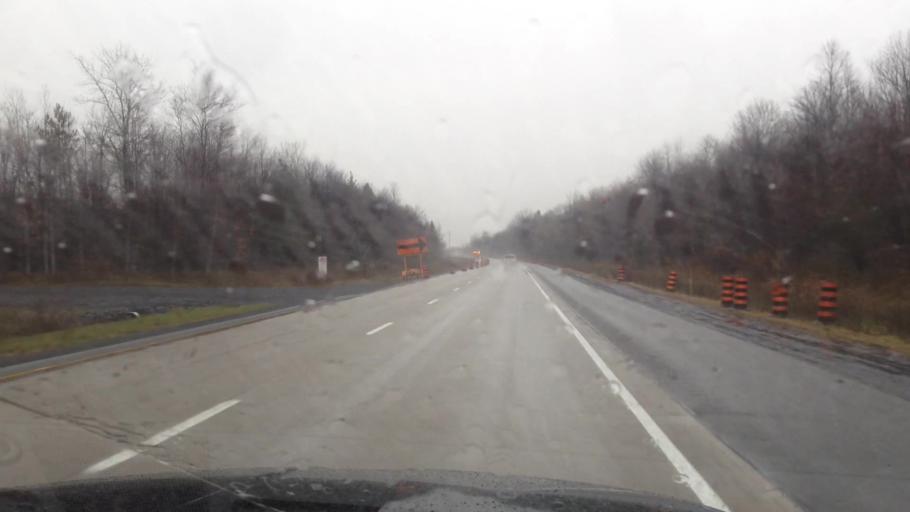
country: CA
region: Ontario
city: Hawkesbury
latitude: 45.4805
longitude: -74.6484
